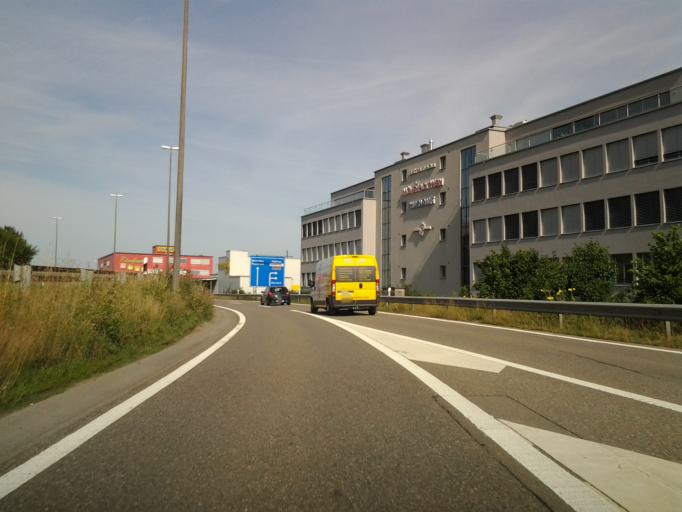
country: CH
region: Schwyz
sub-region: Bezirk March
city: Altendorf
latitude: 47.2012
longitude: 8.7982
